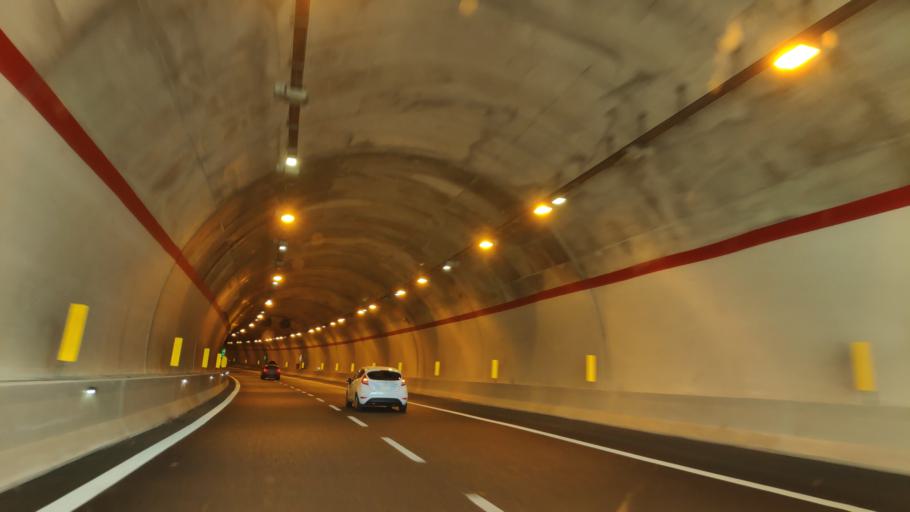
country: IT
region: Calabria
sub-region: Provincia di Cosenza
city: Laino Borgo
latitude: 39.9437
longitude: 15.9593
